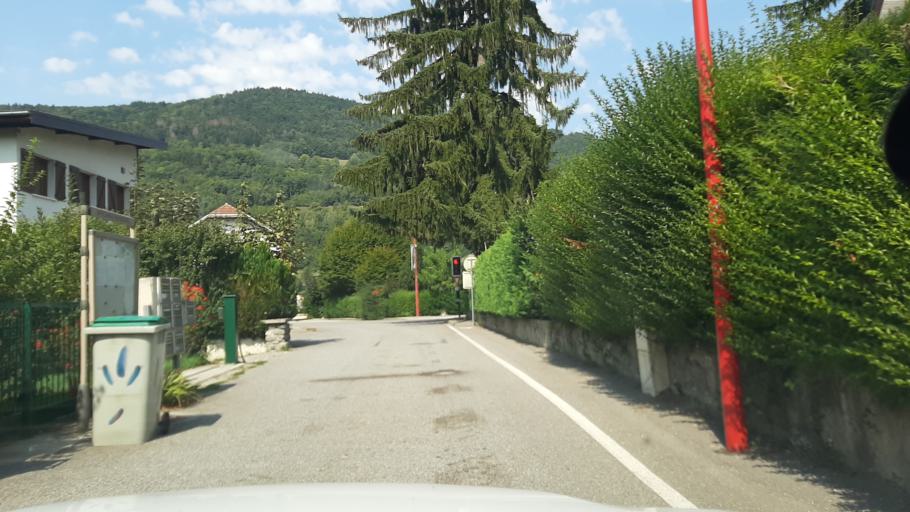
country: FR
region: Rhone-Alpes
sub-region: Departement de la Savoie
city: La Rochette
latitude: 45.4519
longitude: 6.1081
